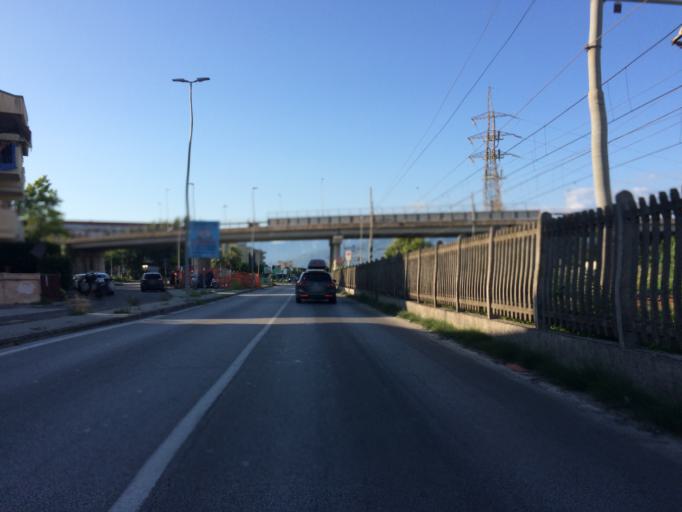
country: IT
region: Tuscany
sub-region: Provincia di Lucca
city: Viareggio
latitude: 43.8805
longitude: 10.2512
